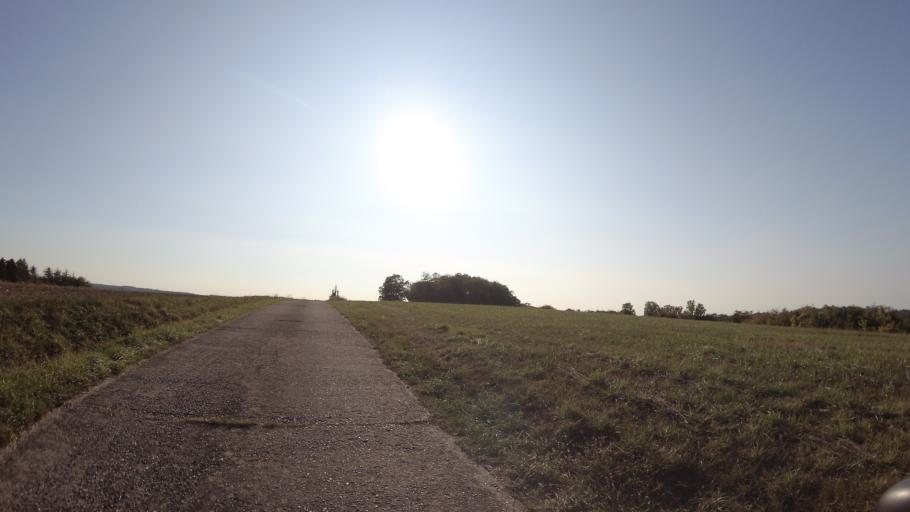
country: DE
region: Saarland
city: Blieskastel
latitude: 49.2301
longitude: 7.2222
